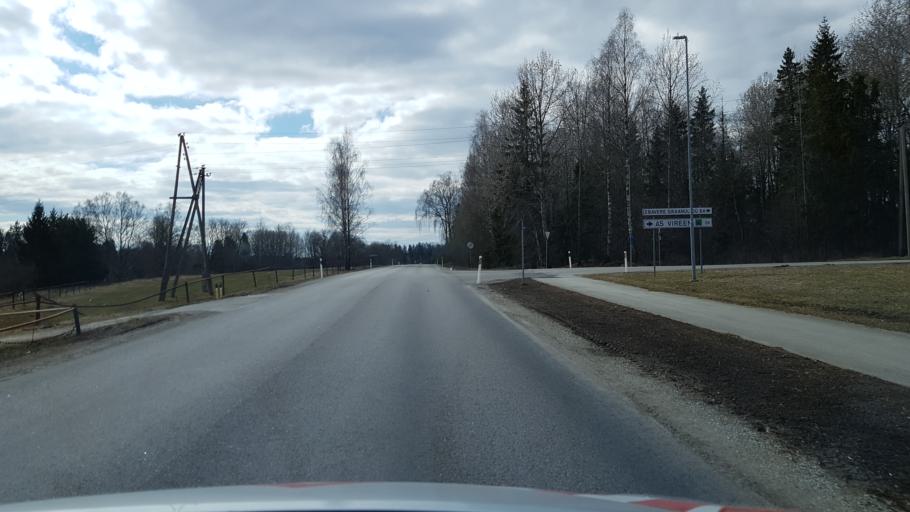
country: EE
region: Laeaene-Virumaa
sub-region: Vaeike-Maarja vald
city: Vaike-Maarja
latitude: 59.1102
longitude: 26.2365
